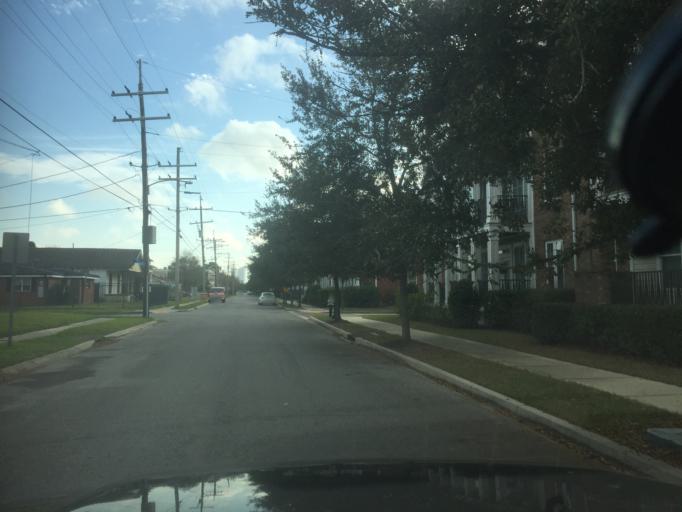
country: US
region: Louisiana
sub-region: Orleans Parish
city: New Orleans
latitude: 29.9974
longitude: -90.0749
